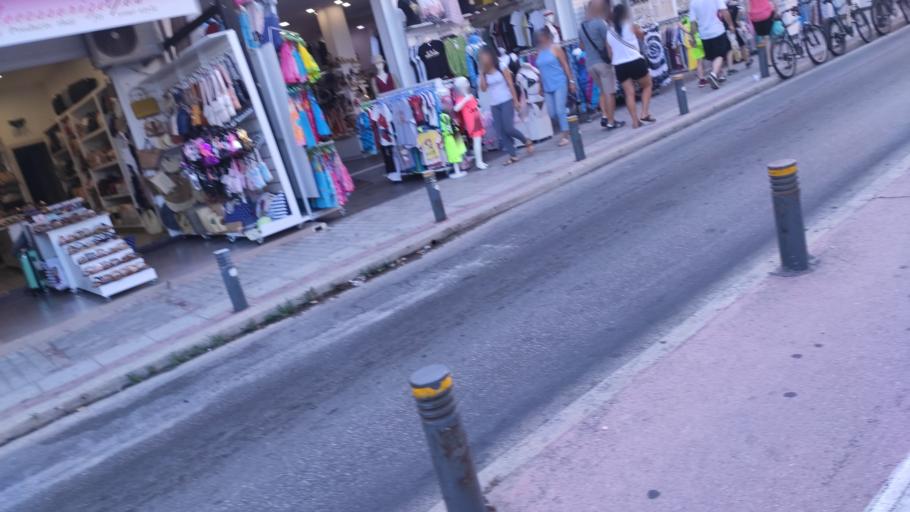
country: GR
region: South Aegean
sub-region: Nomos Dodekanisou
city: Kos
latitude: 36.8964
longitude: 27.2857
